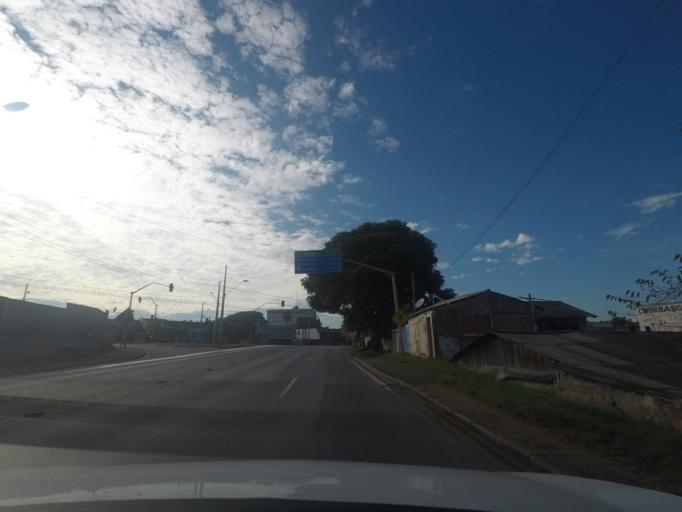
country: BR
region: Parana
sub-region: Curitiba
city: Curitiba
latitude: -25.4421
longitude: -49.2519
